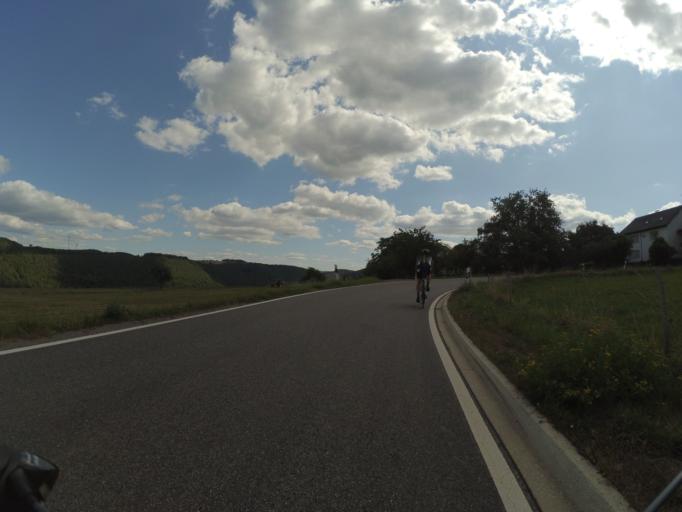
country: DE
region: Rheinland-Pfalz
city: Bescheid
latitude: 49.7638
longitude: 6.8857
